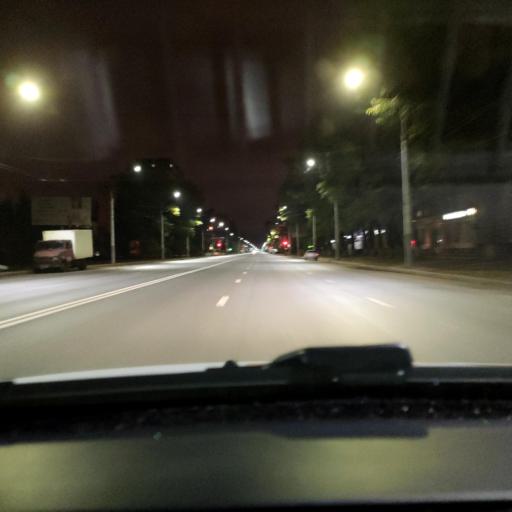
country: RU
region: Voronezj
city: Voronezh
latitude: 51.6448
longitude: 39.2384
